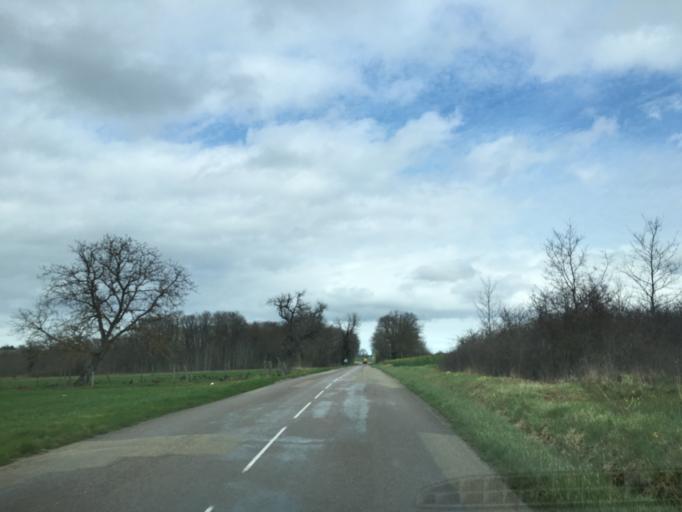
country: FR
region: Bourgogne
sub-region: Departement de l'Yonne
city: Charbuy
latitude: 47.8158
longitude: 3.4499
